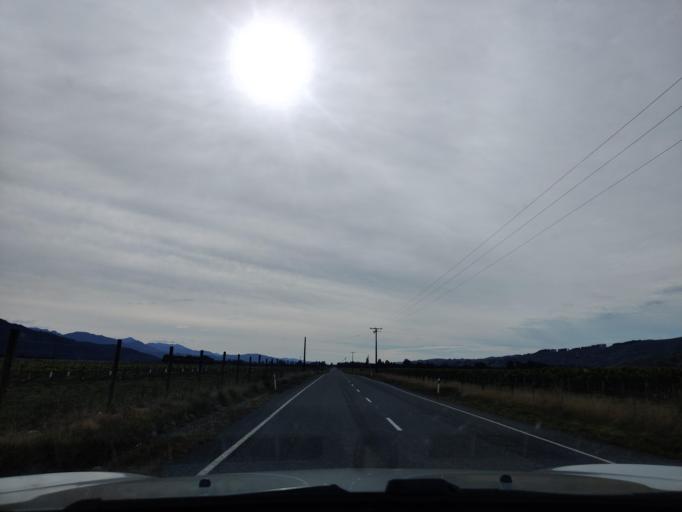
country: NZ
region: Tasman
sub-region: Tasman District
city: Richmond
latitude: -41.6143
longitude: 173.3848
